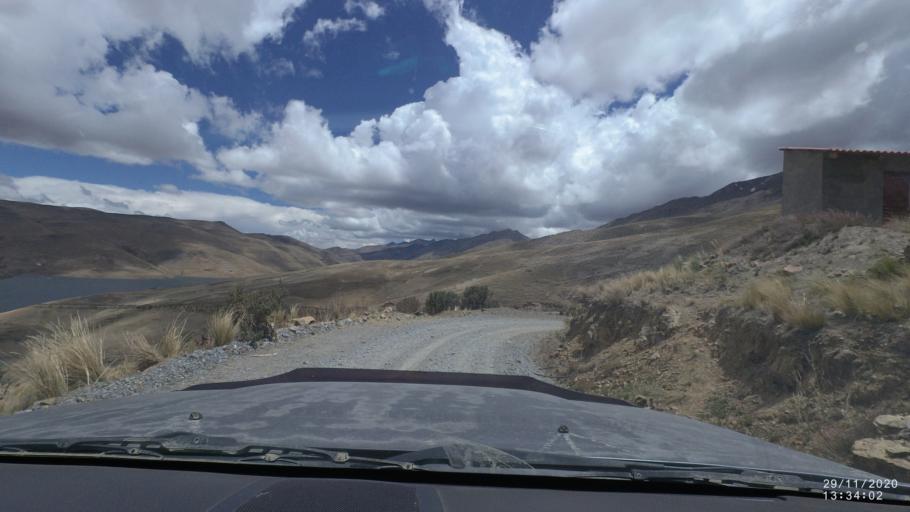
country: BO
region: Cochabamba
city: Cochabamba
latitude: -17.1092
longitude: -66.3363
